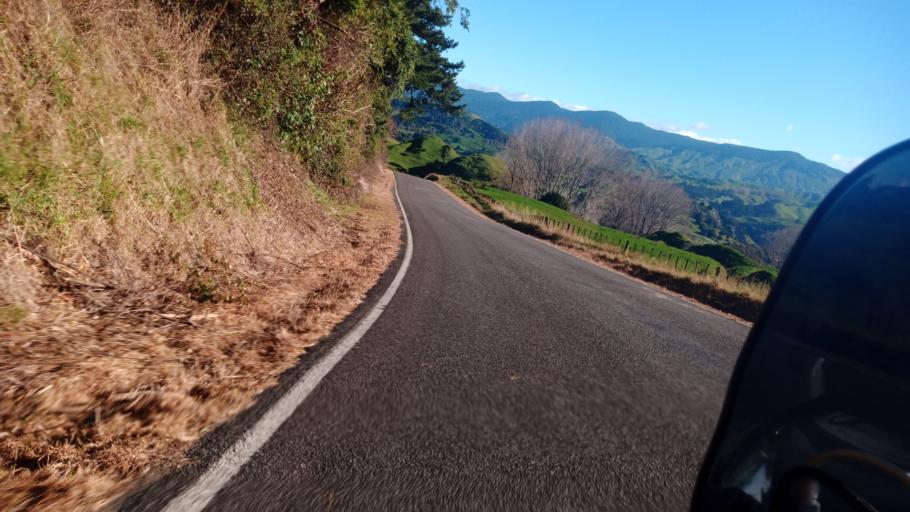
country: NZ
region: Hawke's Bay
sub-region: Wairoa District
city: Wairoa
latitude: -38.8257
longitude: 177.2929
